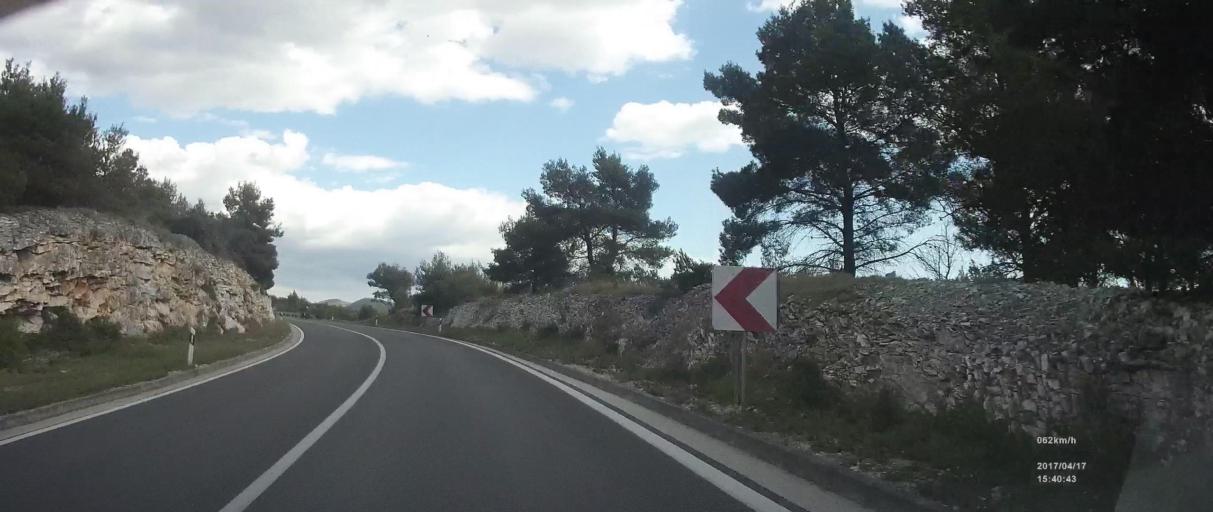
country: HR
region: Sibensko-Kniniska
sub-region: Grad Sibenik
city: Brodarica
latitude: 43.6465
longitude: 15.9510
